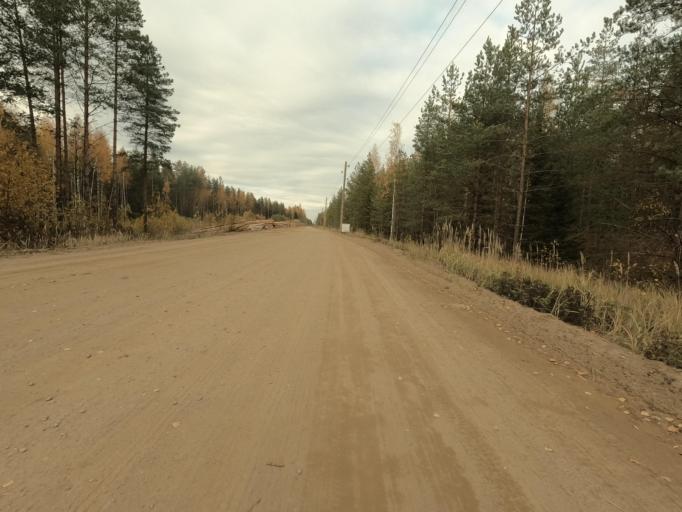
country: RU
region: Leningrad
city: Priladozhskiy
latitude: 59.6895
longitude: 31.3607
